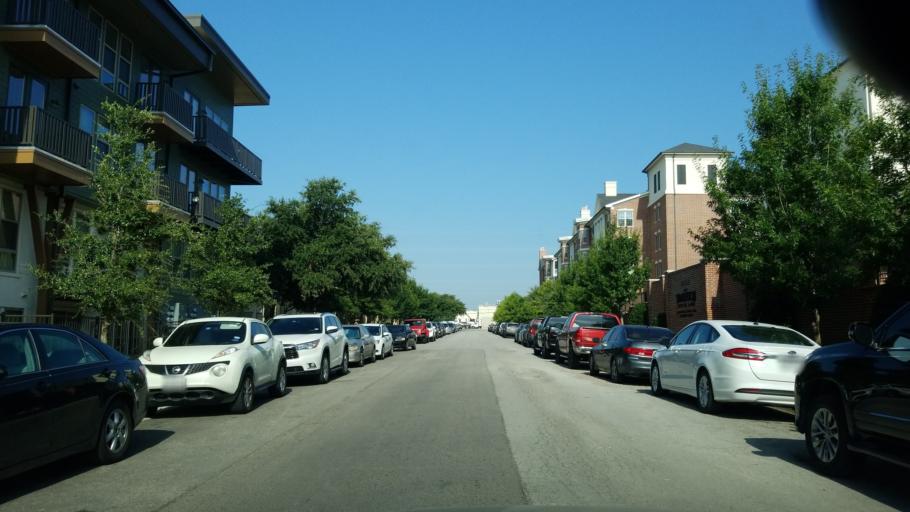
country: US
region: Texas
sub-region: Dallas County
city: Highland Park
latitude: 32.8492
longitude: -96.7657
